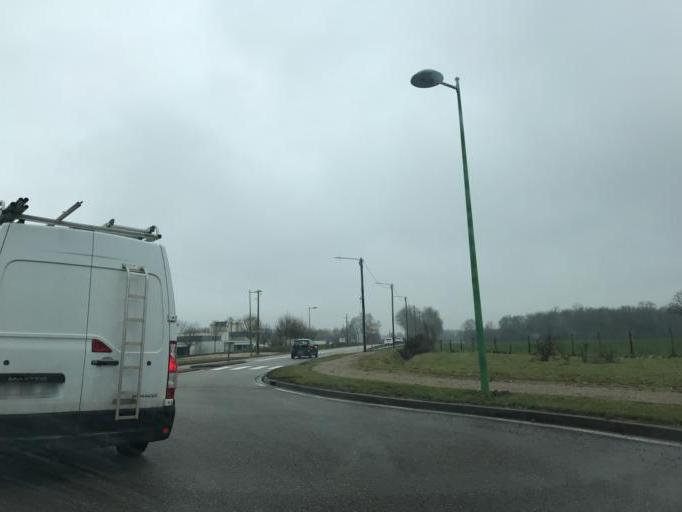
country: FR
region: Rhone-Alpes
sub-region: Departement de l'Ain
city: Servas
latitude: 46.1290
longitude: 5.1617
